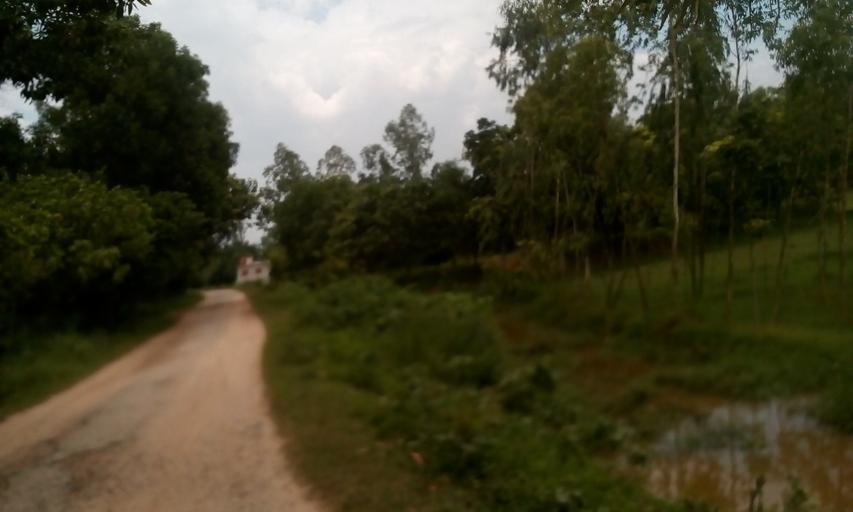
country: BD
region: Rangpur Division
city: Parbatipur
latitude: 25.3994
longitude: 88.9868
